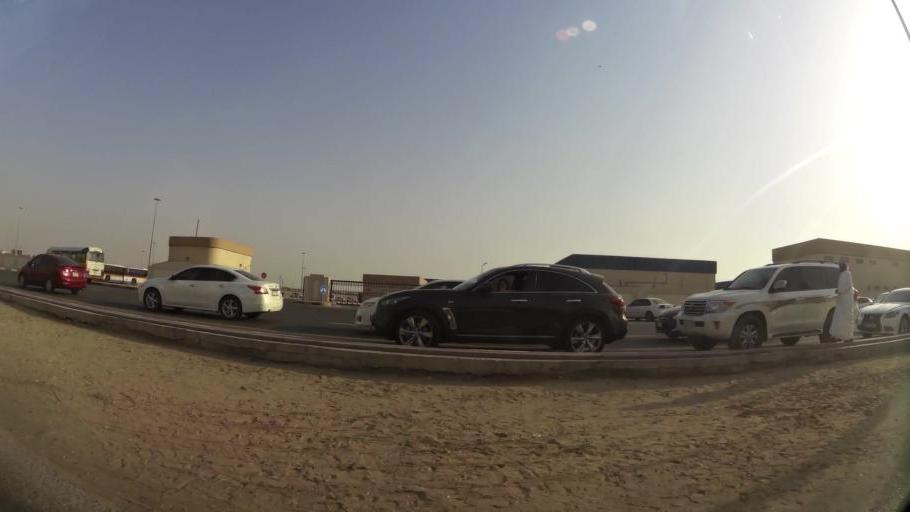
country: AE
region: Ajman
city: Ajman
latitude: 25.3774
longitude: 55.4551
